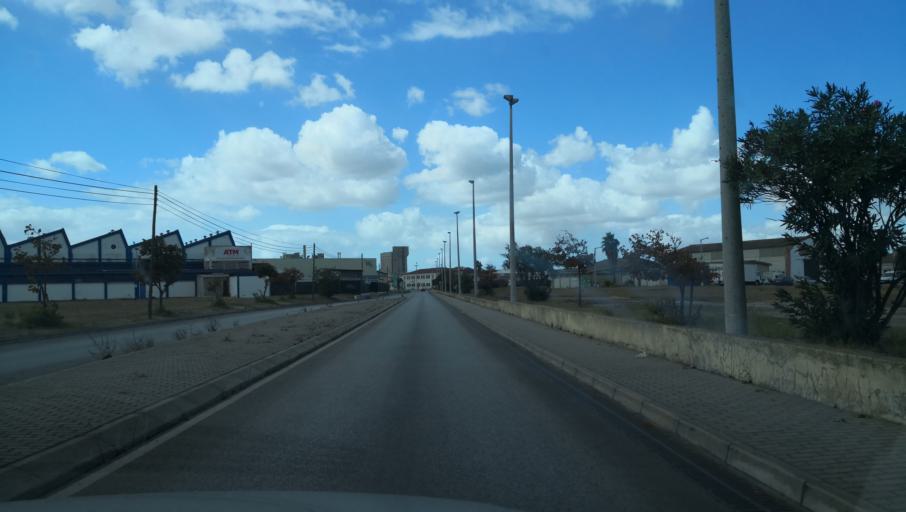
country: PT
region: Setubal
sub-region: Barreiro
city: Barreiro
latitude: 38.6671
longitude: -9.0625
